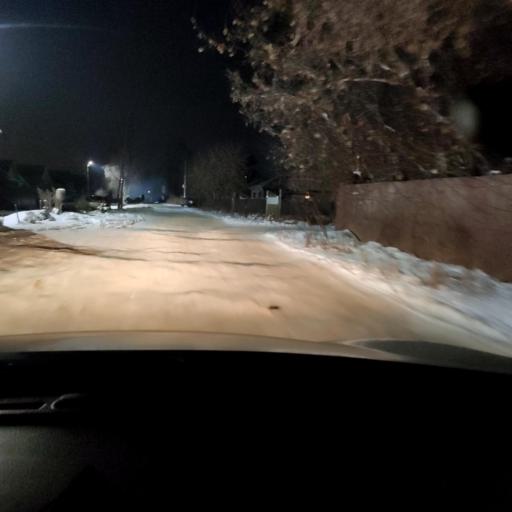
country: RU
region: Tatarstan
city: Stolbishchi
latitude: 55.6487
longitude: 49.2070
